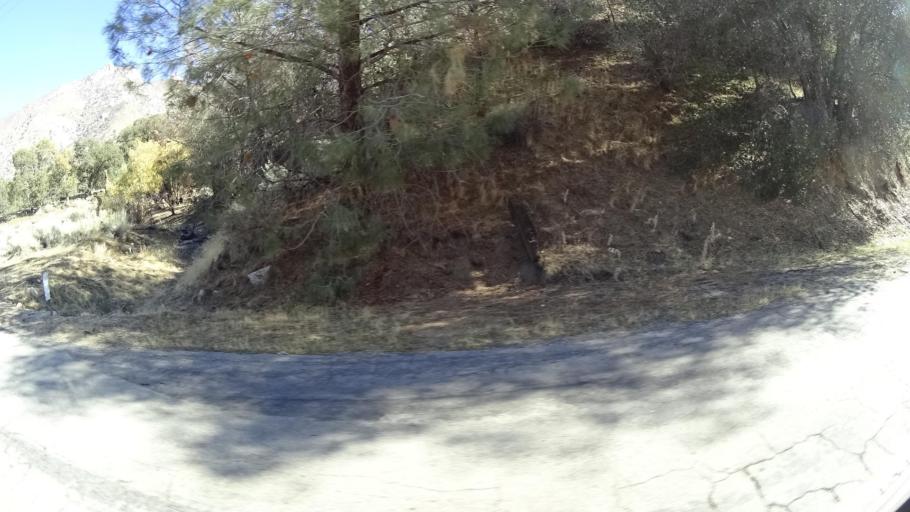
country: US
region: California
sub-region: Kern County
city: Bodfish
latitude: 35.5348
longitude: -118.5112
